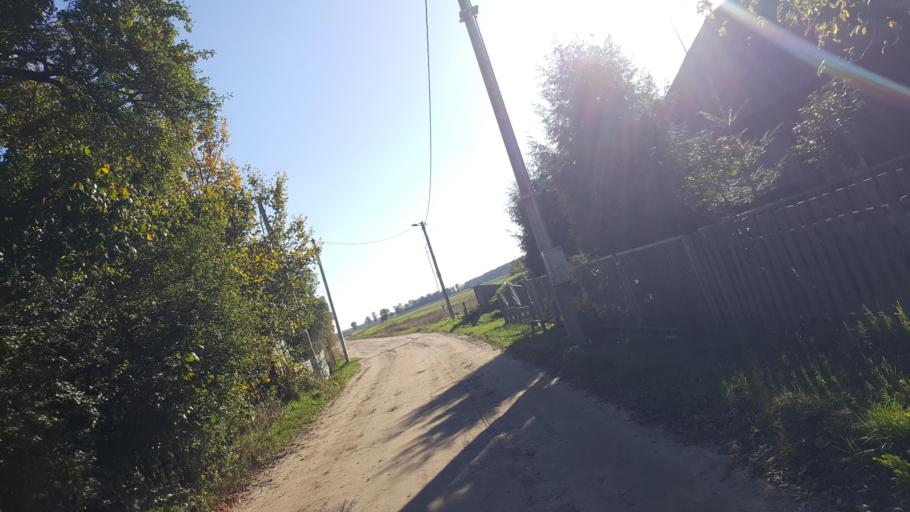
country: BY
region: Brest
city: Kamyanyets
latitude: 52.3869
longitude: 23.8845
